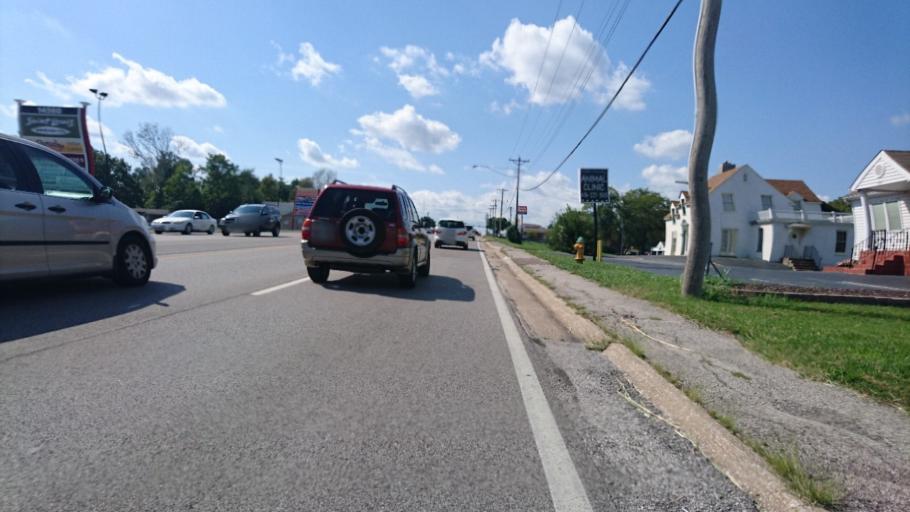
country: US
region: Missouri
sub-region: Saint Louis County
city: Winchester
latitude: 38.5931
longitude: -90.5259
